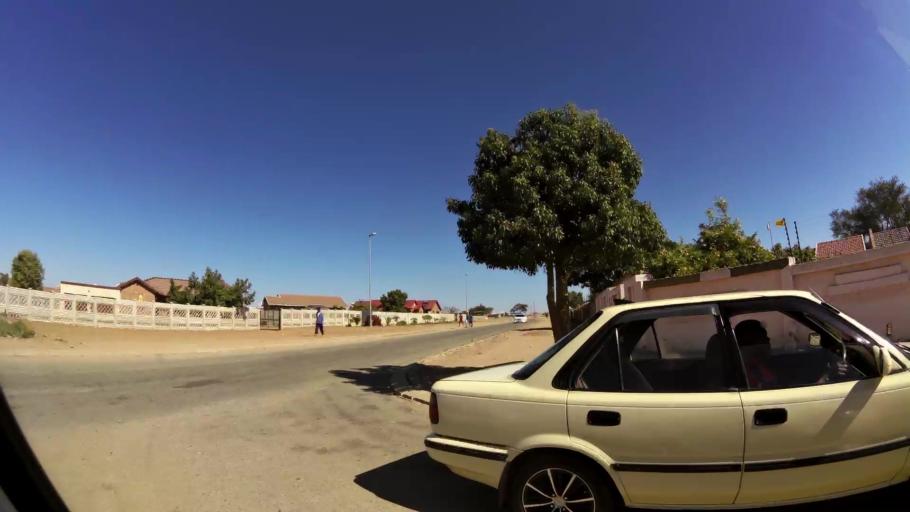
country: ZA
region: Limpopo
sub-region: Capricorn District Municipality
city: Polokwane
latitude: -23.8686
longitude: 29.4277
